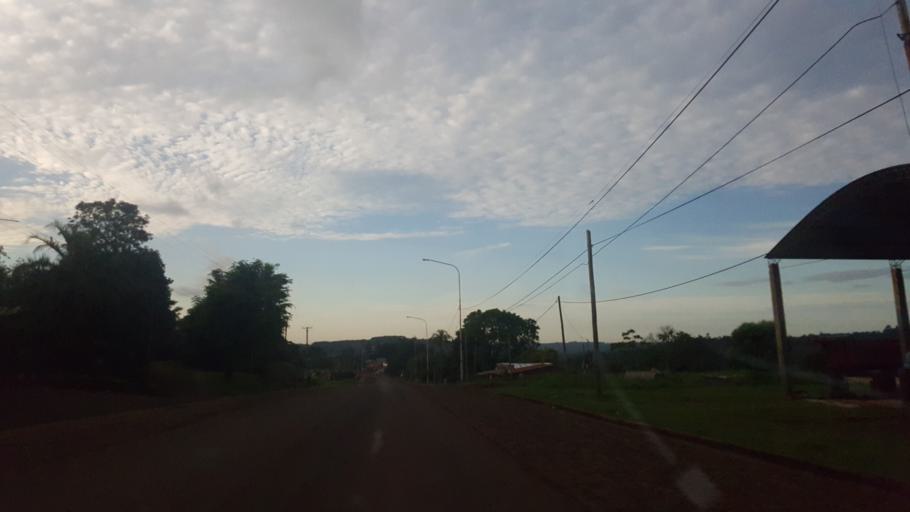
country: AR
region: Misiones
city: Dos de Mayo
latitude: -27.0318
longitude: -54.6859
